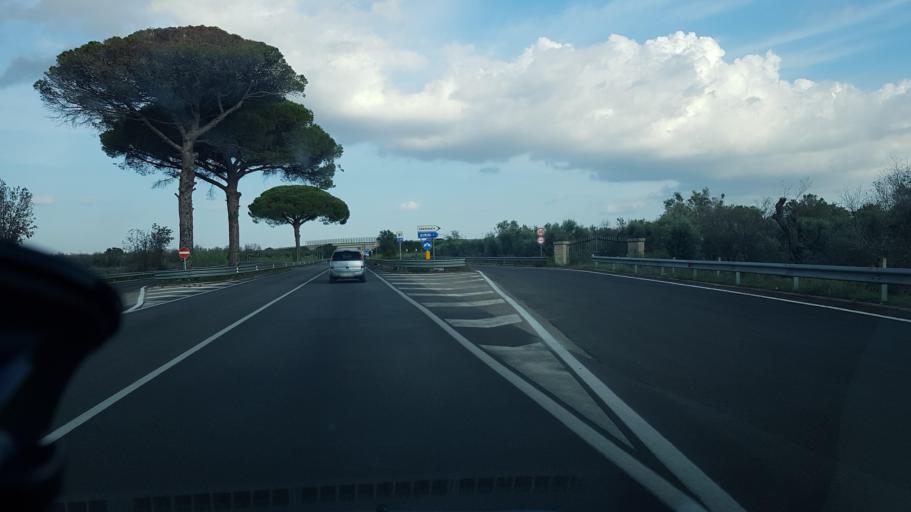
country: IT
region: Apulia
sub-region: Provincia di Lecce
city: Gemini
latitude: 39.9218
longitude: 18.1881
